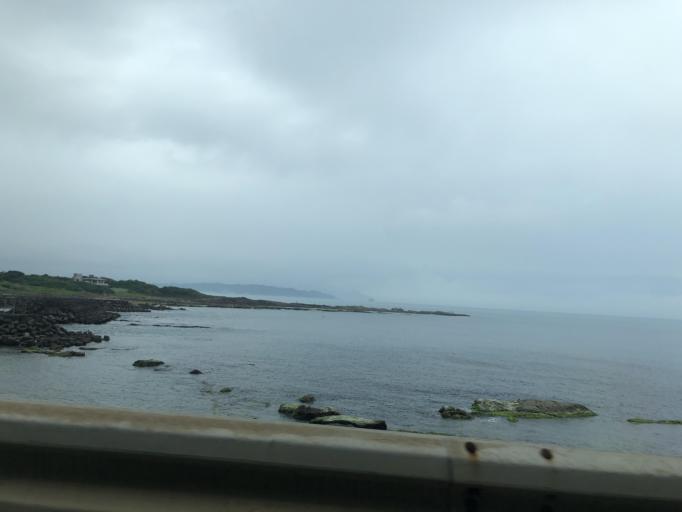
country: TW
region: Taiwan
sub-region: Keelung
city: Keelung
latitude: 25.2023
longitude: 121.6800
